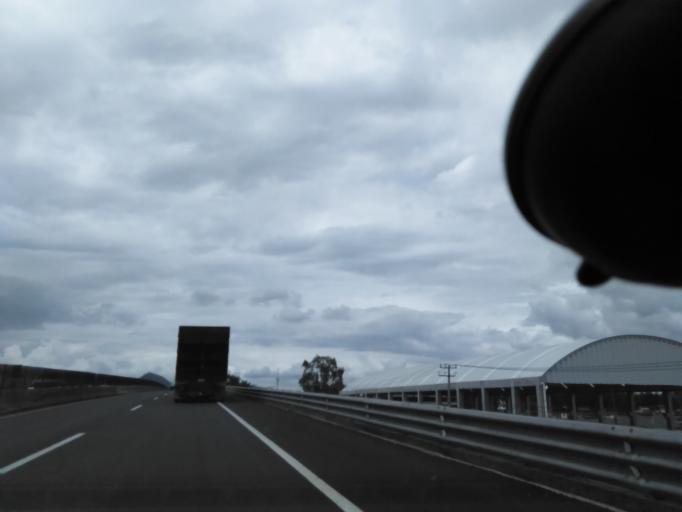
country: MX
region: Morelos
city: San Pedro Xalpa
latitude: 19.8108
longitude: -99.1919
